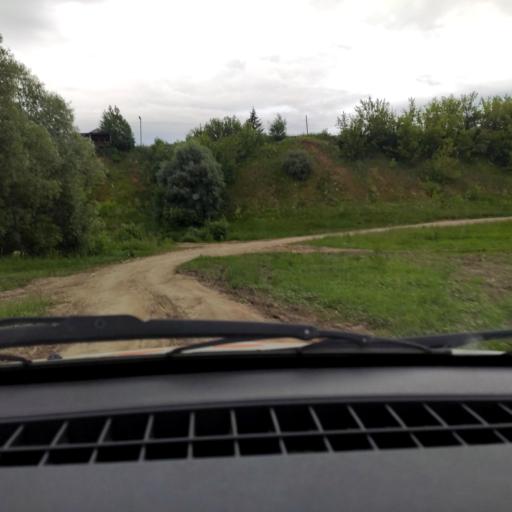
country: RU
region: Bashkortostan
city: Iglino
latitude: 54.7955
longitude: 56.2318
